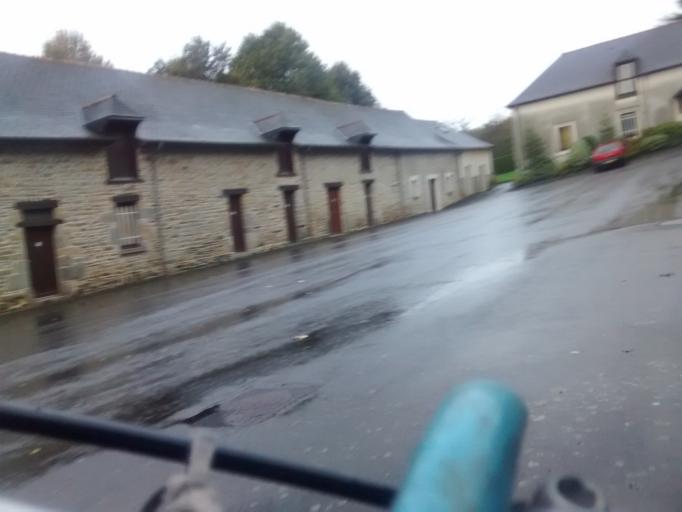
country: FR
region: Brittany
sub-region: Departement d'Ille-et-Vilaine
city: Cesson-Sevigne
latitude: 48.1185
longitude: -1.6176
